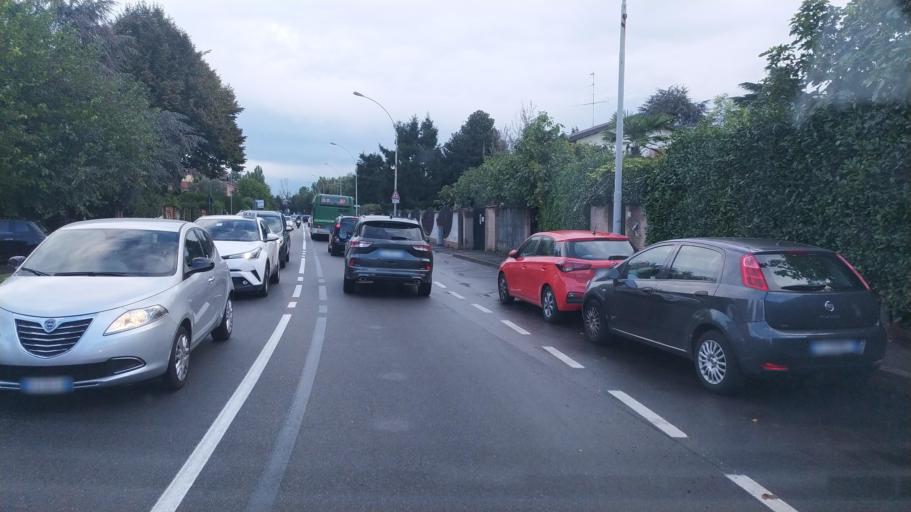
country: IT
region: Lombardy
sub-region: Citta metropolitana di Milano
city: Trezzano sul Naviglio
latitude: 45.4294
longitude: 9.0572
